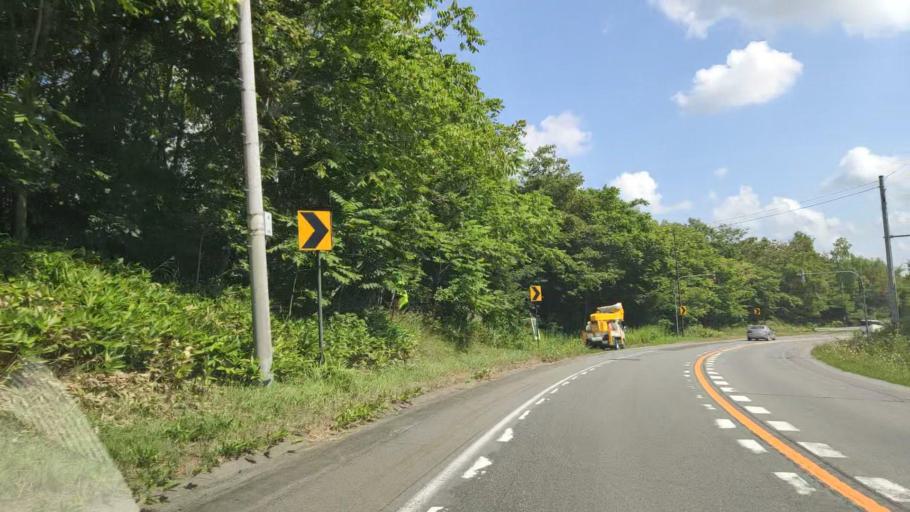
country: JP
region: Hokkaido
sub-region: Asahikawa-shi
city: Asahikawa
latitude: 43.5834
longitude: 142.4375
